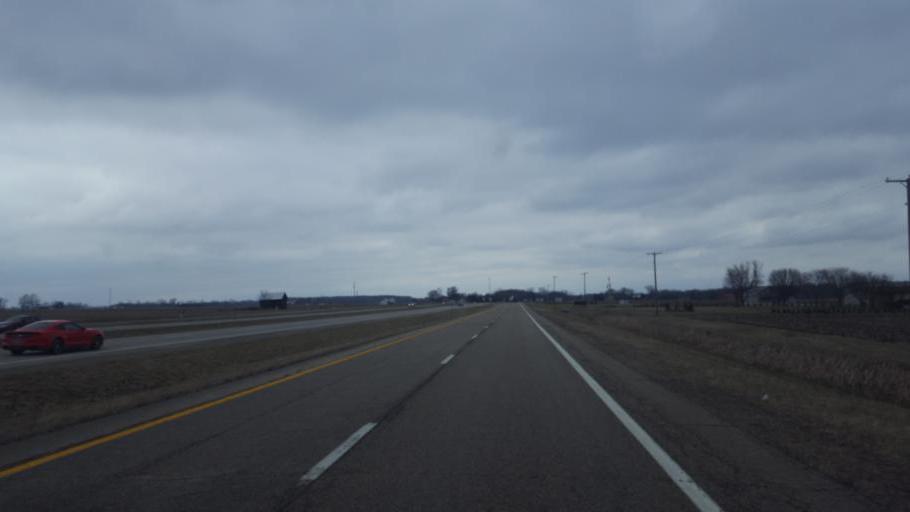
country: US
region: Ohio
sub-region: Marion County
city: Prospect
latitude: 40.4202
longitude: -83.0740
